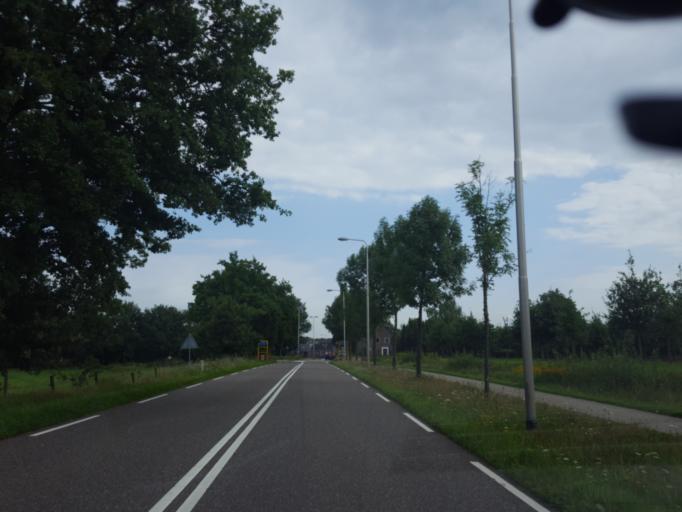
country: NL
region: Limburg
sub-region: Gemeente Bergen
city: Wellerlooi
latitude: 51.5177
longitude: 6.0808
